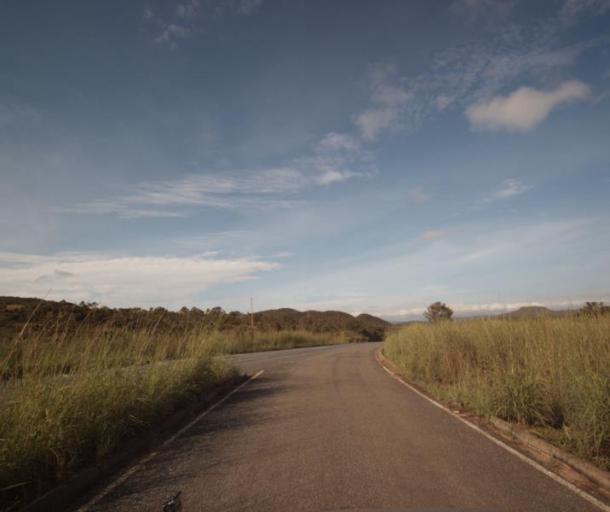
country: BR
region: Goias
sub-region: Pirenopolis
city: Pirenopolis
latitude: -15.5783
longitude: -48.6266
